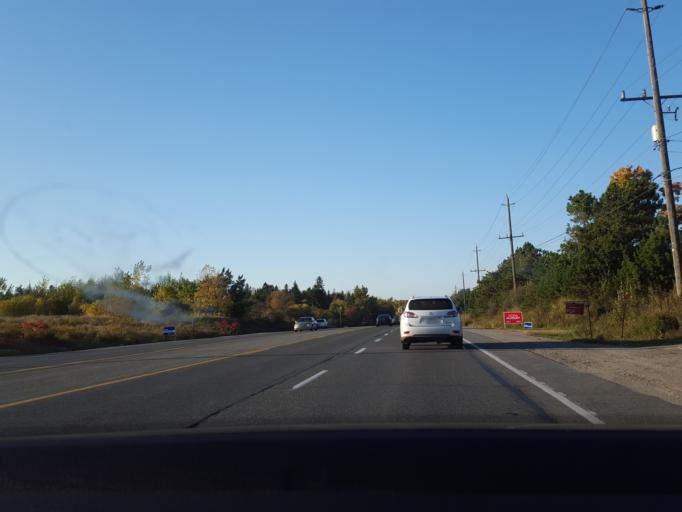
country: CA
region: Ontario
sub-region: York
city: Richmond Hill
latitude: 43.9296
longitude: -79.4516
